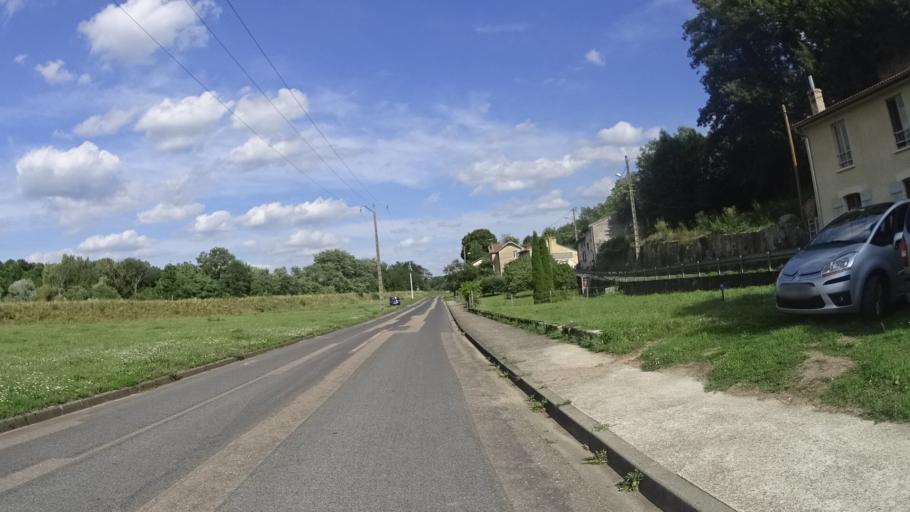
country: FR
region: Lorraine
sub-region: Departement de Meurthe-et-Moselle
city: Dommartin-les-Toul
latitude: 48.6435
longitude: 5.9349
